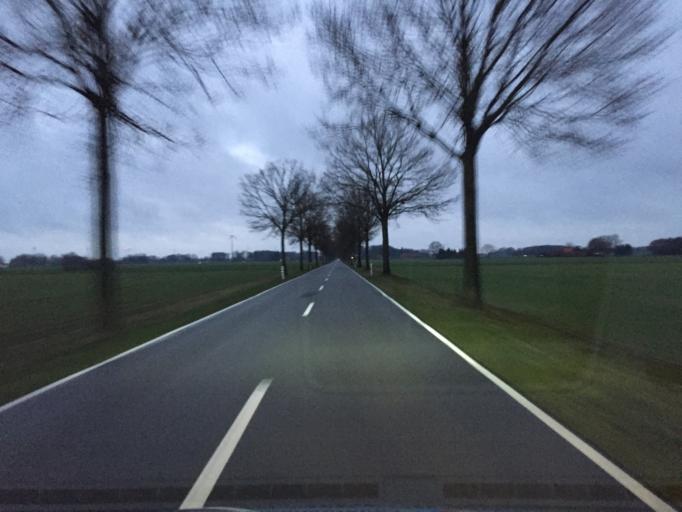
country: DE
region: Lower Saxony
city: Schwaforden
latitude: 52.7625
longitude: 8.8318
